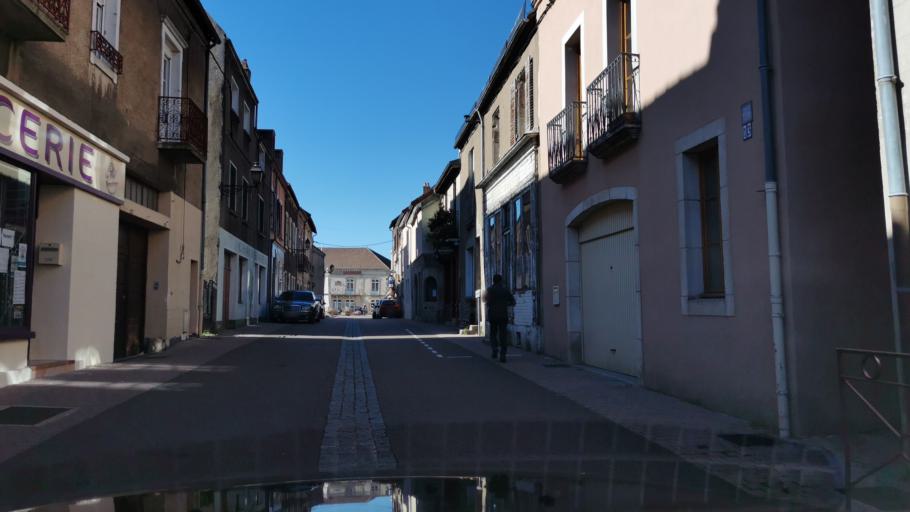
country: FR
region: Bourgogne
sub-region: Departement de Saone-et-Loire
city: Montcenis
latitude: 46.7896
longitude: 4.3887
